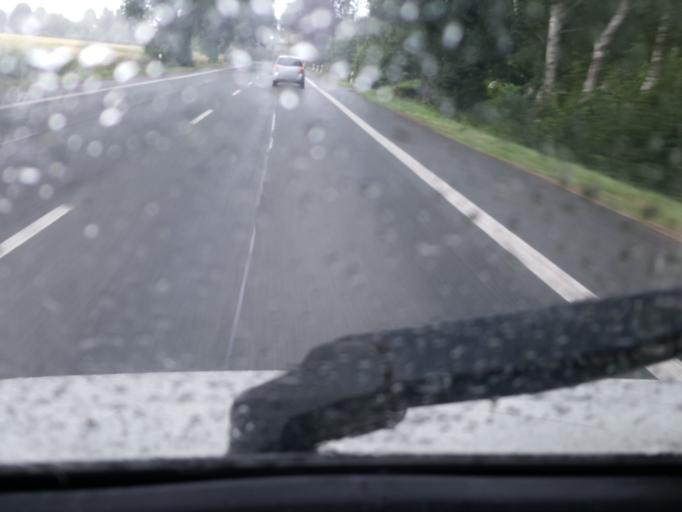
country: DE
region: North Rhine-Westphalia
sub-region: Regierungsbezirk Detmold
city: Petershagen
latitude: 52.3384
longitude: 8.9358
